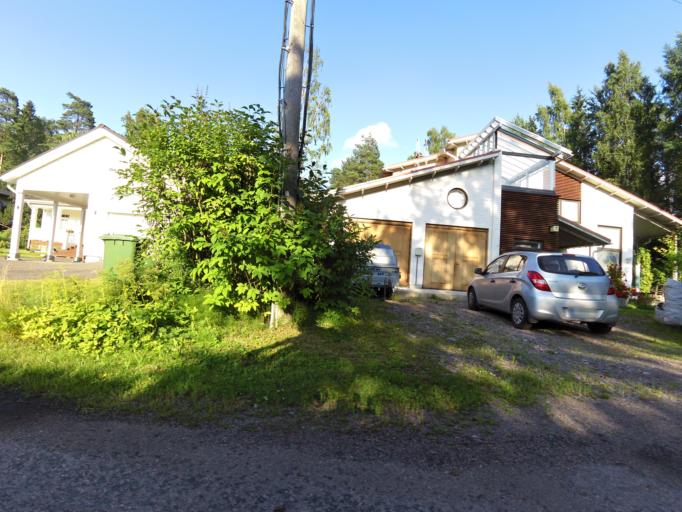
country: FI
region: Uusimaa
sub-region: Helsinki
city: Espoo
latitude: 60.1620
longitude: 24.6430
